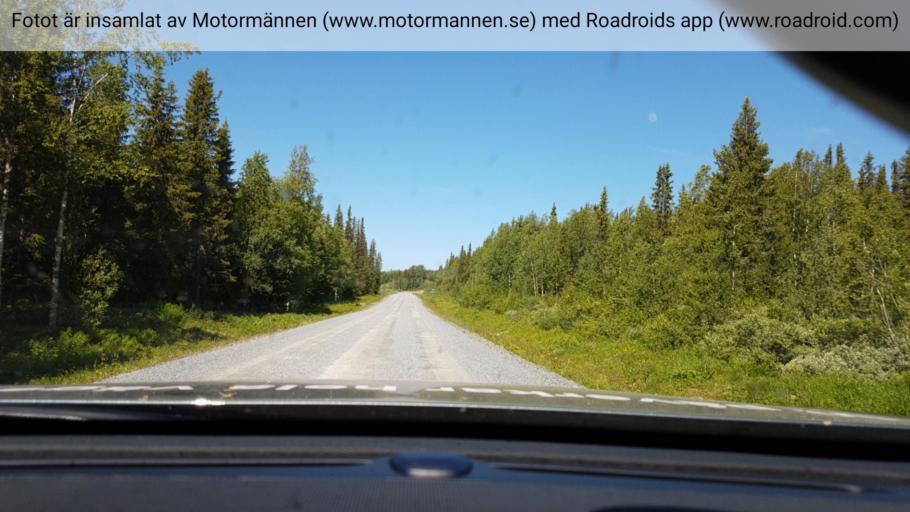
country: SE
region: Vaesterbotten
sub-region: Vilhelmina Kommun
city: Sjoberg
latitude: 64.7300
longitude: 15.7828
